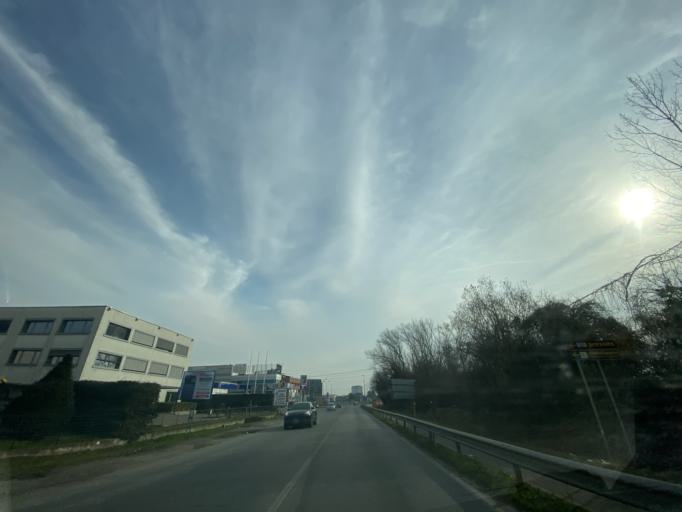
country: IT
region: Lombardy
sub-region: Citta metropolitana di Milano
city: Carugate
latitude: 45.5410
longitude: 9.3361
